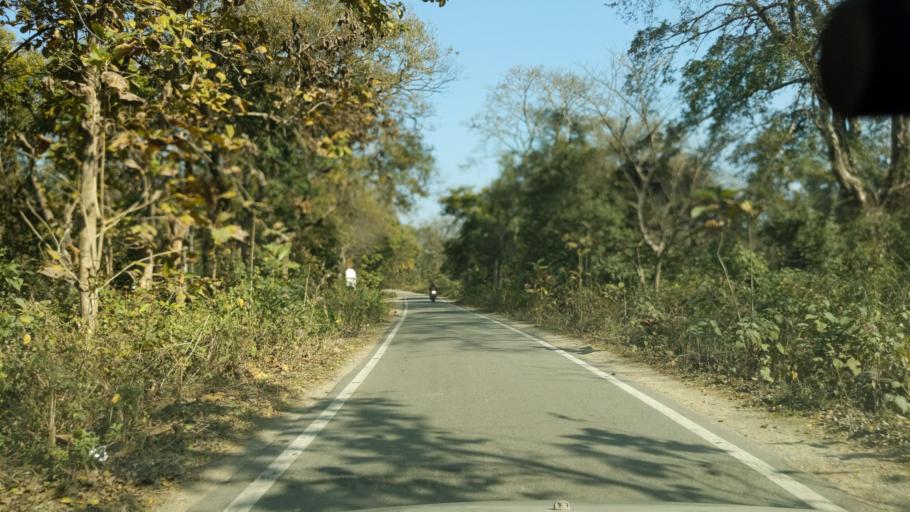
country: IN
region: Uttarakhand
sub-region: Naini Tal
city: Ramnagar
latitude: 29.4117
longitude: 79.1376
